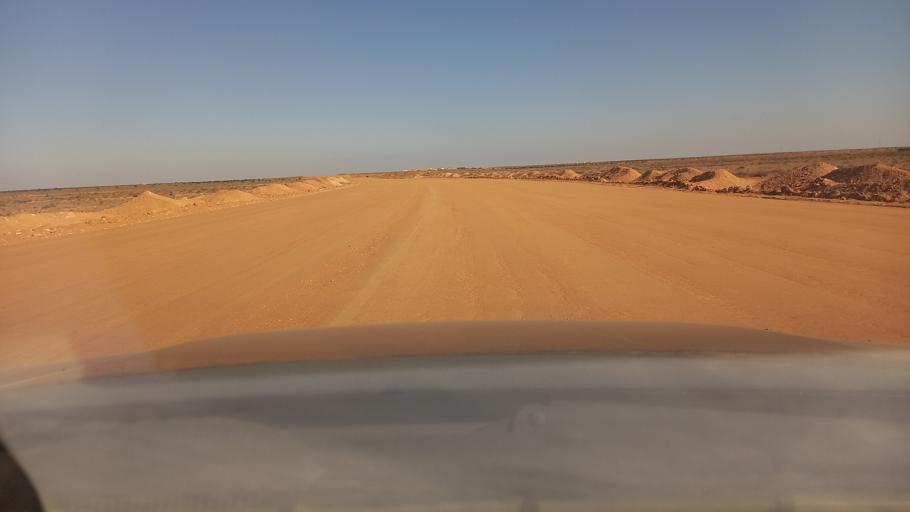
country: TN
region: Madanin
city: Medenine
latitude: 33.1678
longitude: 10.5245
